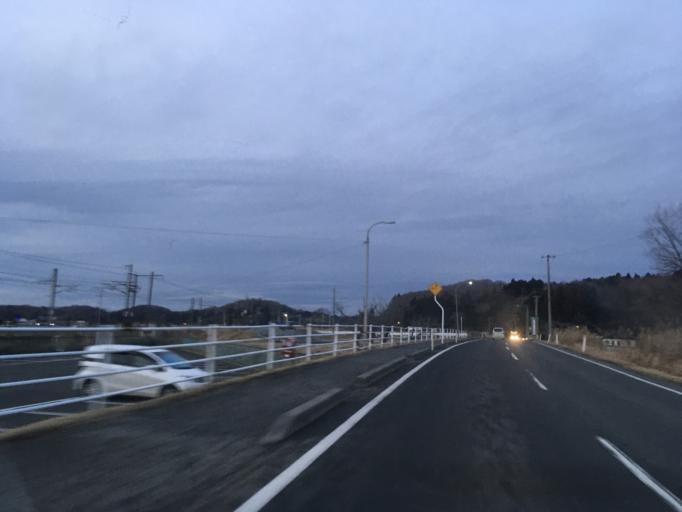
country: JP
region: Miyagi
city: Kogota
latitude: 38.6594
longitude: 141.0735
